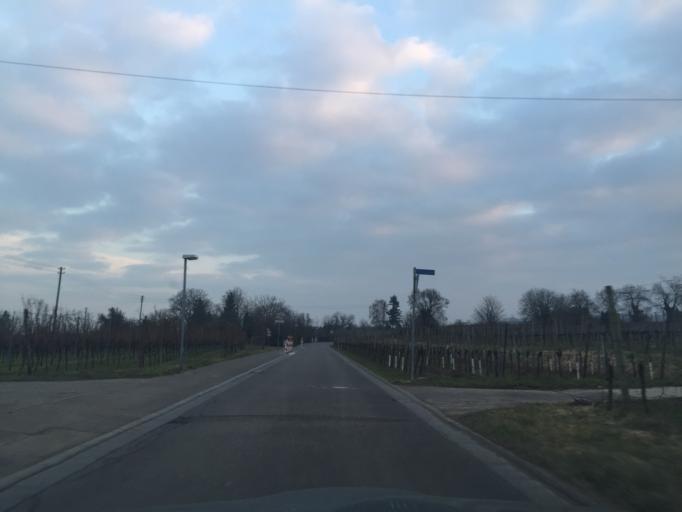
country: DE
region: Baden-Wuerttemberg
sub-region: Karlsruhe Region
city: Schriesheim
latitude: 49.5062
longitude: 8.6618
